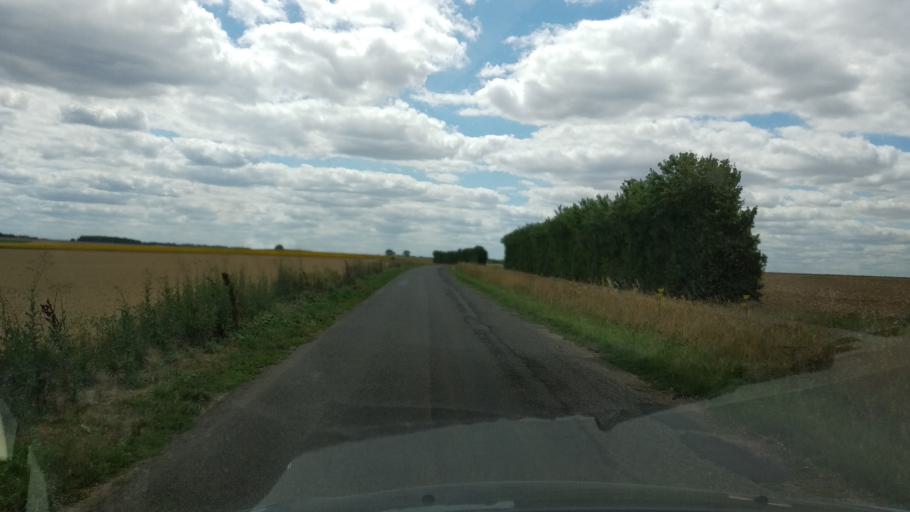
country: FR
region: Poitou-Charentes
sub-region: Departement de la Vienne
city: Jaunay-Clan
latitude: 46.6767
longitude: 0.3418
